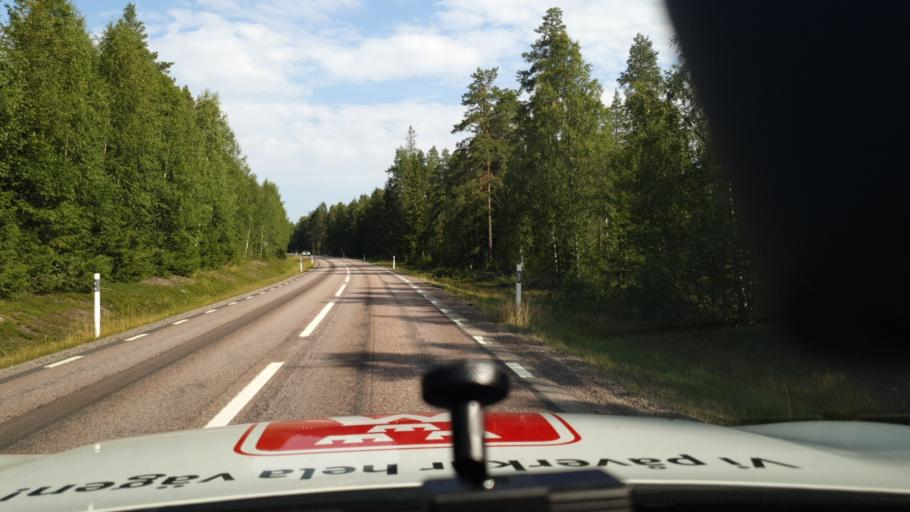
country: SE
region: Vaermland
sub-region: Hagfors Kommun
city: Ekshaerad
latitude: 60.4902
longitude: 13.4127
